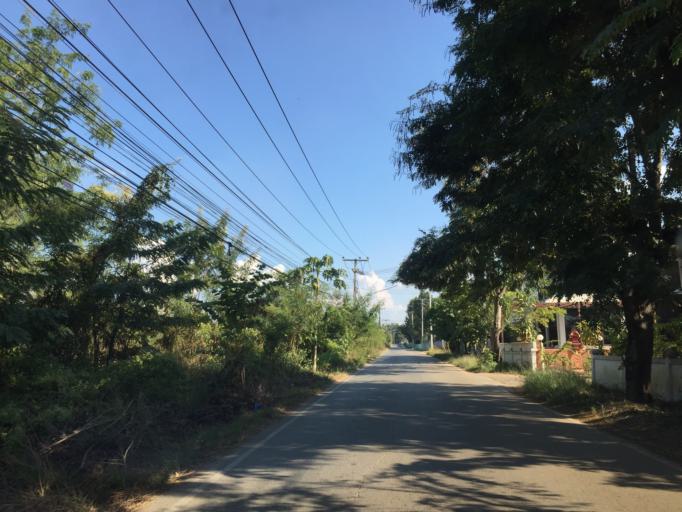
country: TH
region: Lamphun
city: Lamphun
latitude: 18.5709
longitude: 99.0398
